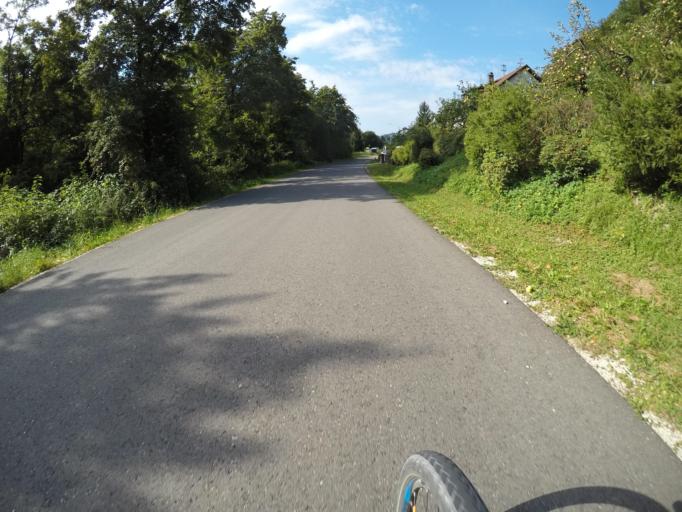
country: DE
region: Baden-Wuerttemberg
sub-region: Regierungsbezirk Stuttgart
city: Geislingen an der Steige
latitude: 48.6313
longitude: 9.8527
